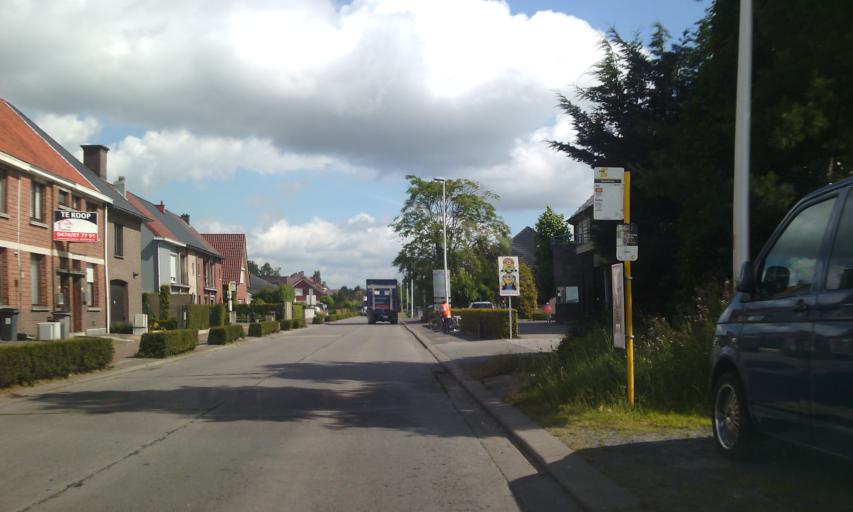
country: BE
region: Flanders
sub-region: Provincie Oost-Vlaanderen
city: Lokeren
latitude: 51.1121
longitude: 3.9614
